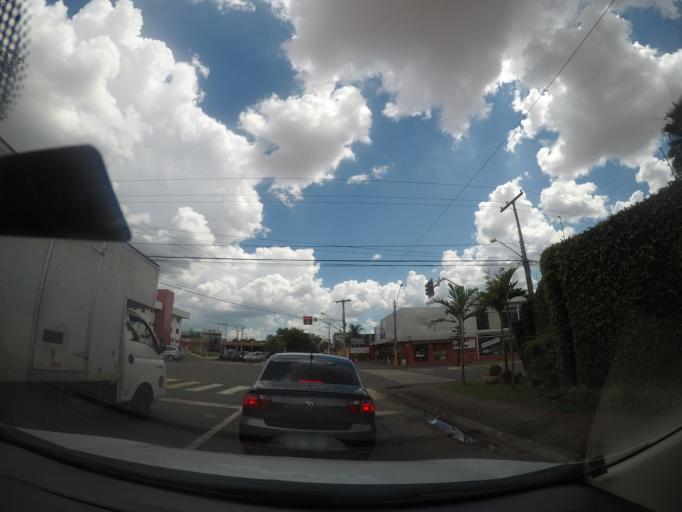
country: BR
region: Goias
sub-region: Goiania
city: Goiania
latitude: -16.7003
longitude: -49.2815
